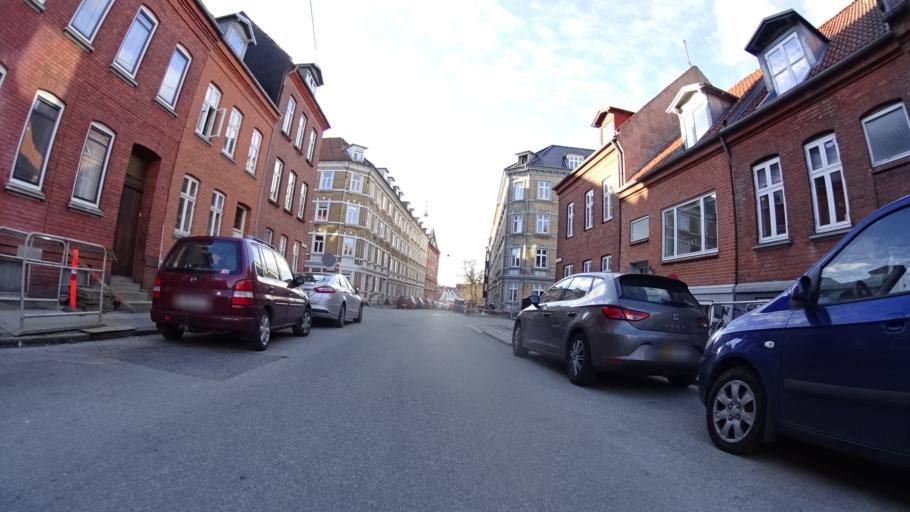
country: DK
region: Central Jutland
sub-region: Arhus Kommune
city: Arhus
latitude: 56.1462
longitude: 10.2005
